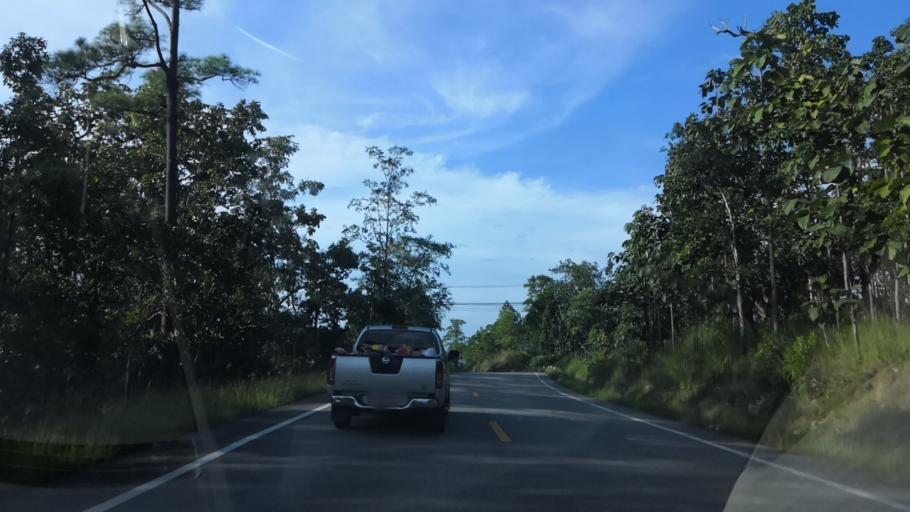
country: TH
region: Mae Hong Son
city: Khun Yuam
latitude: 18.7830
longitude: 97.9388
